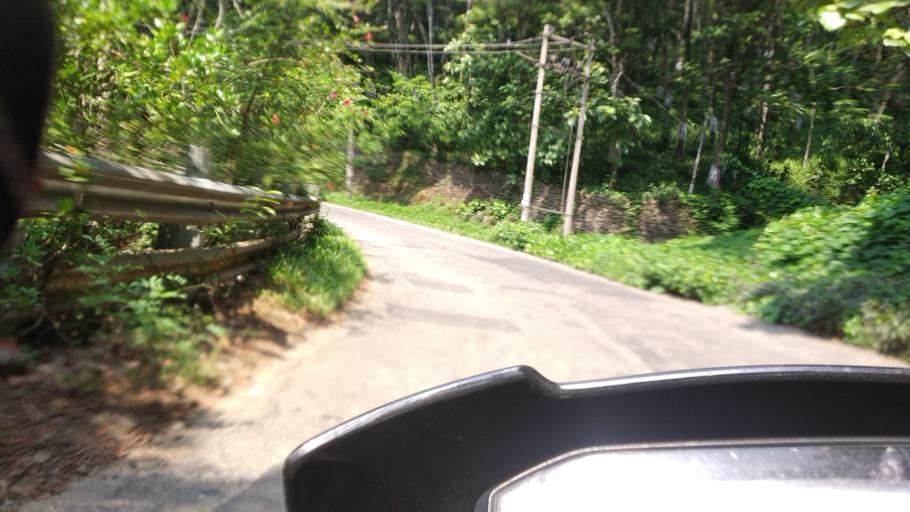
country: IN
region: Kerala
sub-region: Kottayam
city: Erattupetta
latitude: 9.6961
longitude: 76.8228
